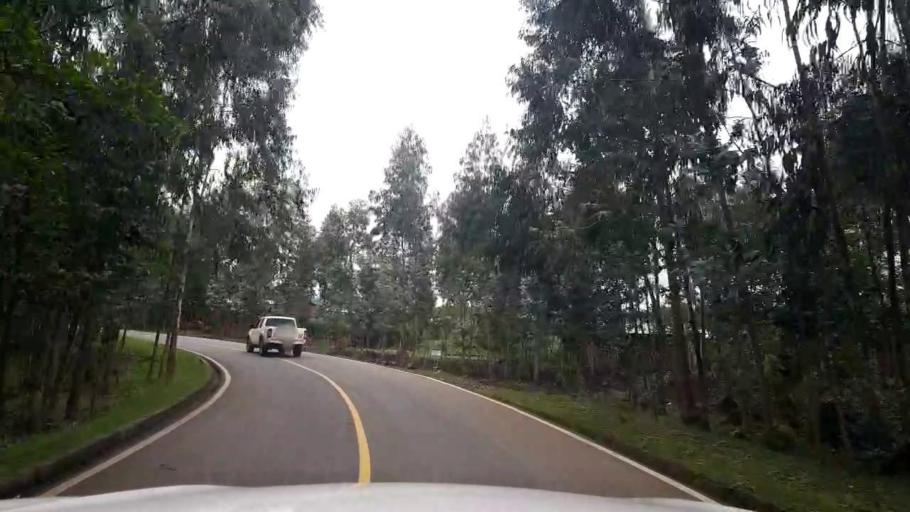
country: RW
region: Northern Province
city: Musanze
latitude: -1.4367
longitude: 29.5513
